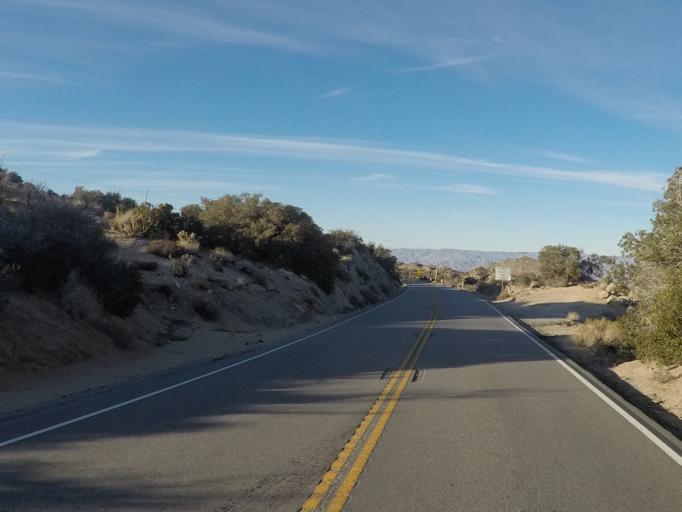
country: US
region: California
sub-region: Riverside County
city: La Quinta
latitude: 33.5969
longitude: -116.4216
